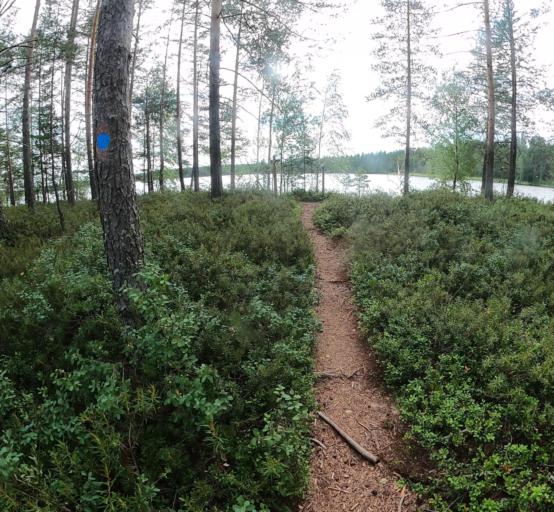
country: FI
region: North Karelia
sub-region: Joensuu
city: Joensuu
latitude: 62.6403
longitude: 29.8250
